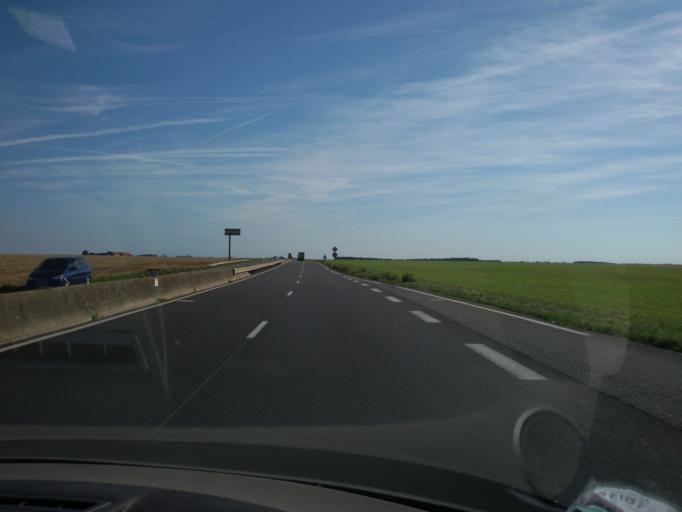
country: FR
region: Ile-de-France
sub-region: Departement de l'Essonne
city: Angerville
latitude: 48.3228
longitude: 2.0131
